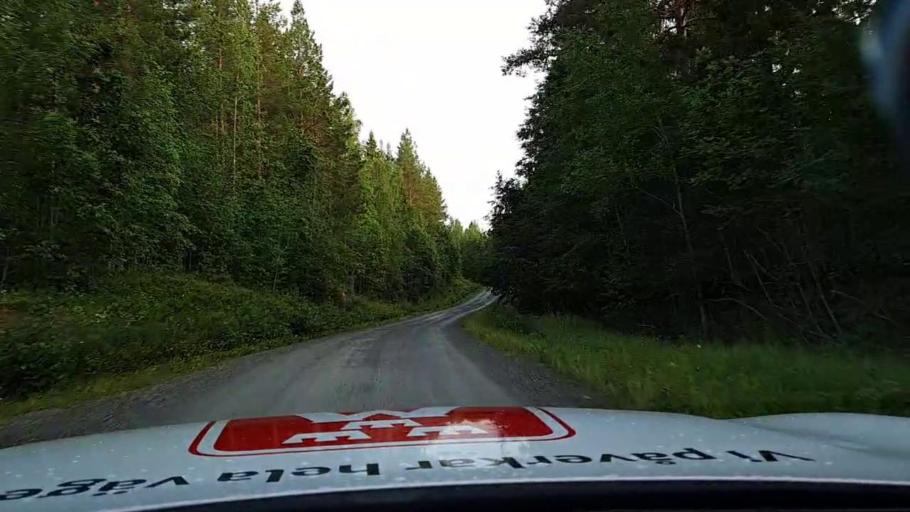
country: SE
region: Jaemtland
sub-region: Bergs Kommun
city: Hoverberg
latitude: 62.8478
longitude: 14.5675
